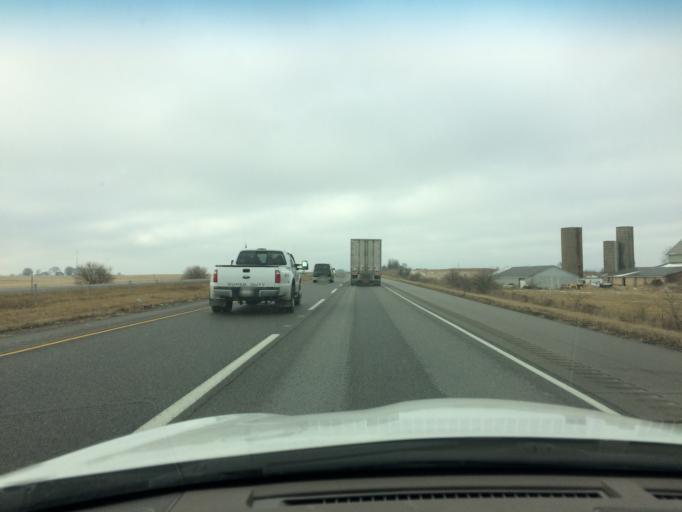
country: US
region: Illinois
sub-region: Kane County
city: Maple Park
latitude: 41.8699
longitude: -88.5854
